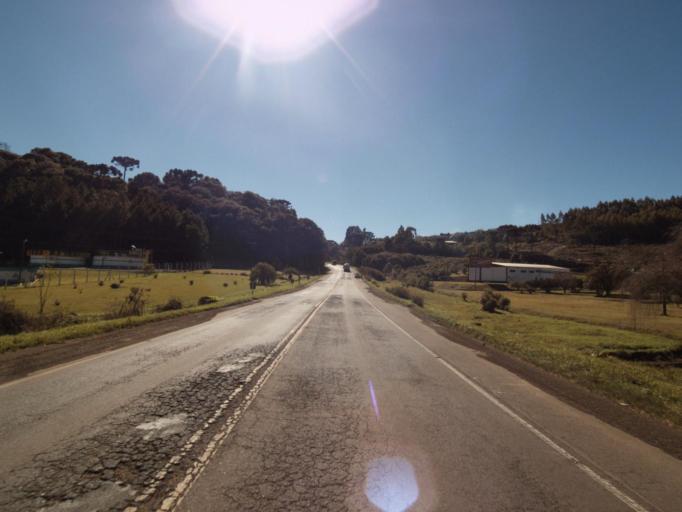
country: BR
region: Santa Catarina
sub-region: Joacaba
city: Joacaba
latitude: -27.0801
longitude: -51.6639
